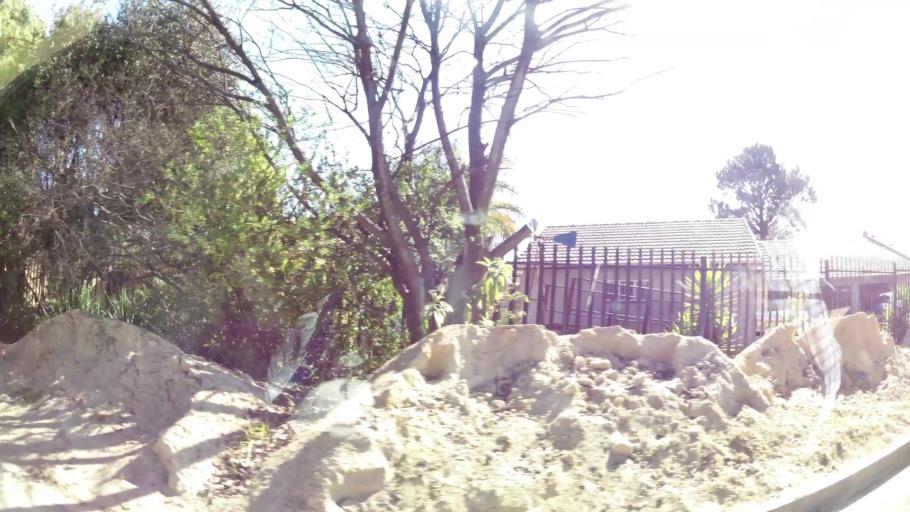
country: ZA
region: Gauteng
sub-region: City of Johannesburg Metropolitan Municipality
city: Modderfontein
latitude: -26.0571
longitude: 28.2038
